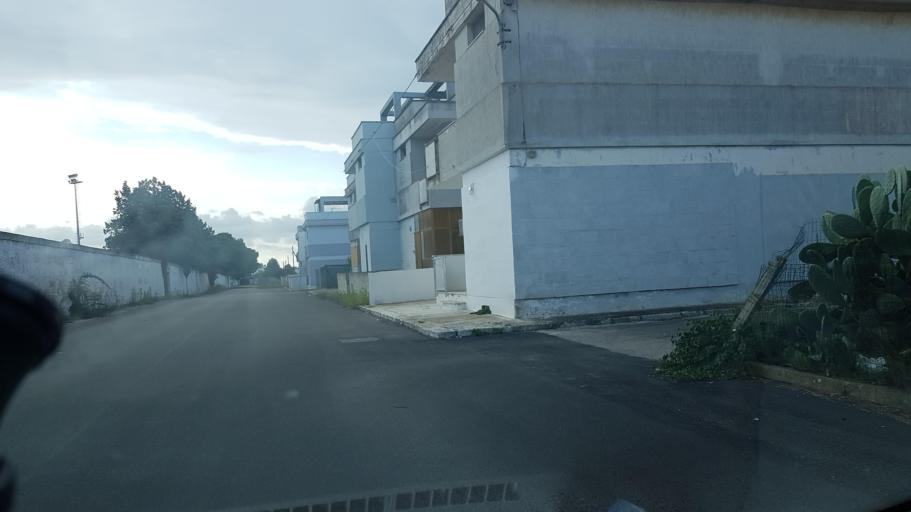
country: IT
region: Apulia
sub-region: Provincia di Brindisi
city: San Pietro Vernotico
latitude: 40.4872
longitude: 18.0046
